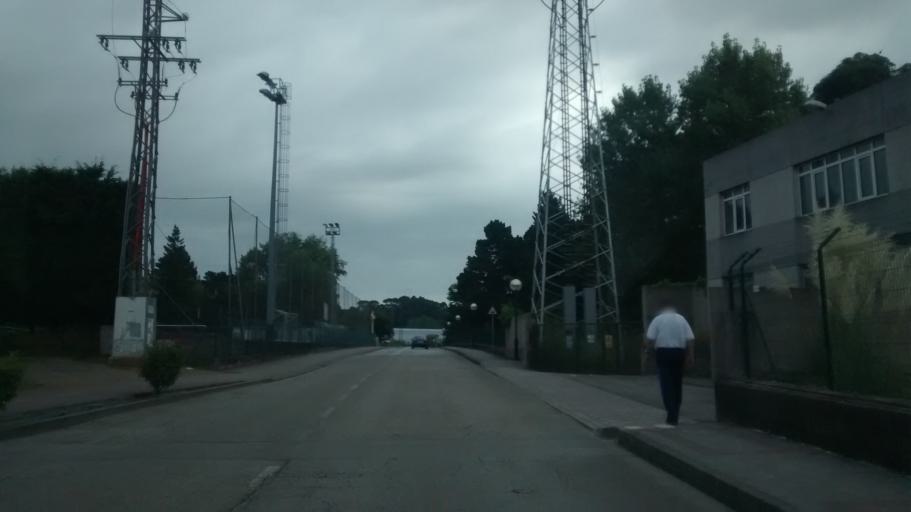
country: ES
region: Cantabria
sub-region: Provincia de Cantabria
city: El Astillero
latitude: 43.4147
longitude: -3.8240
